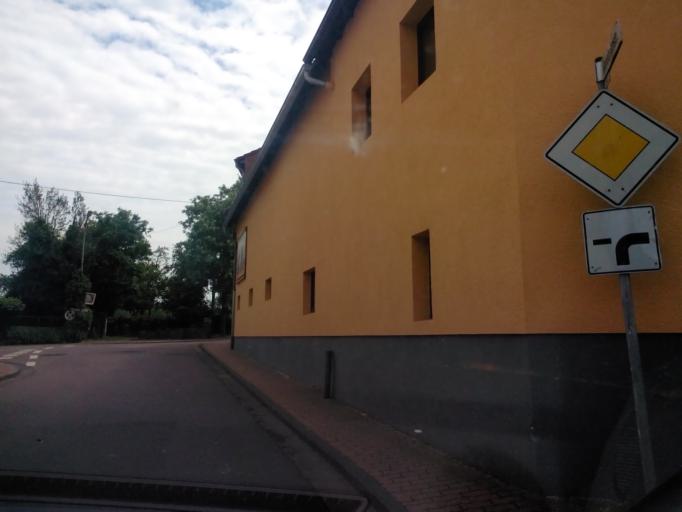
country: DE
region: Saarland
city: Lebach
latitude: 49.4079
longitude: 6.8949
